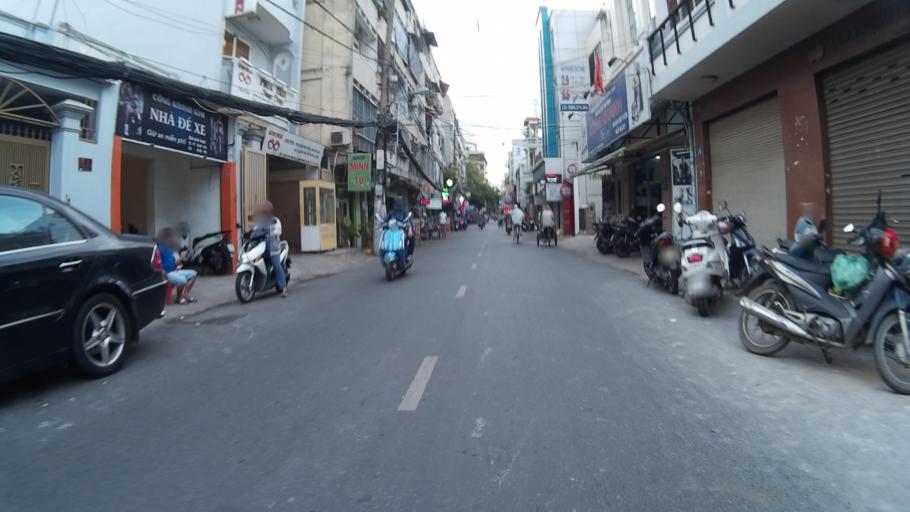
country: VN
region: Ho Chi Minh City
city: Quan Binh Thanh
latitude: 10.7957
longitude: 106.6957
